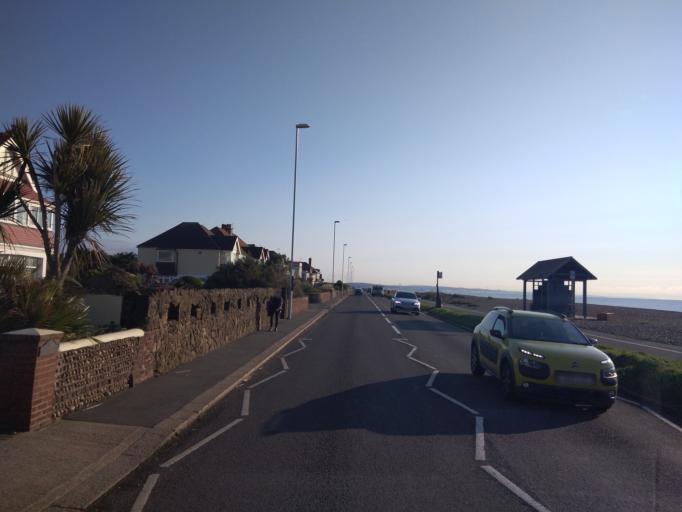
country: GB
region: England
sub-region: West Sussex
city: Worthing
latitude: 50.8140
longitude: -0.3481
